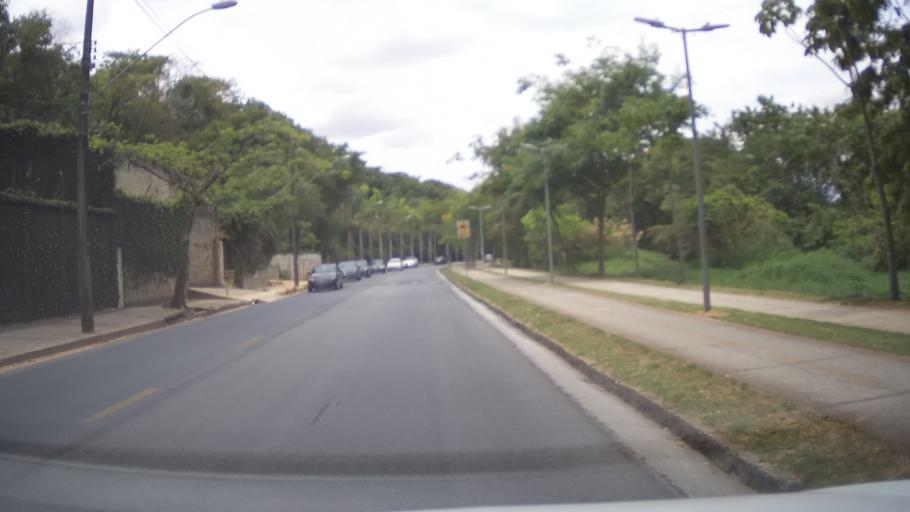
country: BR
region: Minas Gerais
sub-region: Belo Horizonte
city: Belo Horizonte
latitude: -19.8504
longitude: -44.0013
